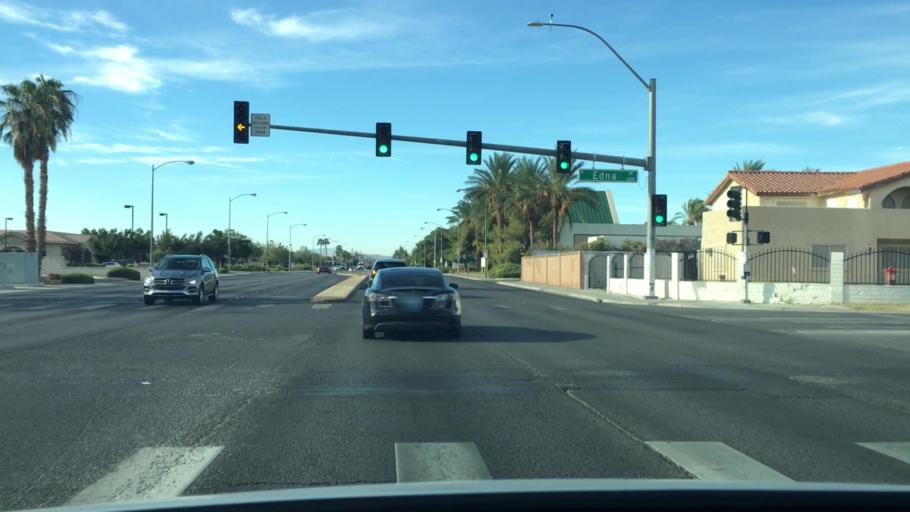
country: US
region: Nevada
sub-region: Clark County
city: Spring Valley
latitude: 36.1366
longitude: -115.2234
